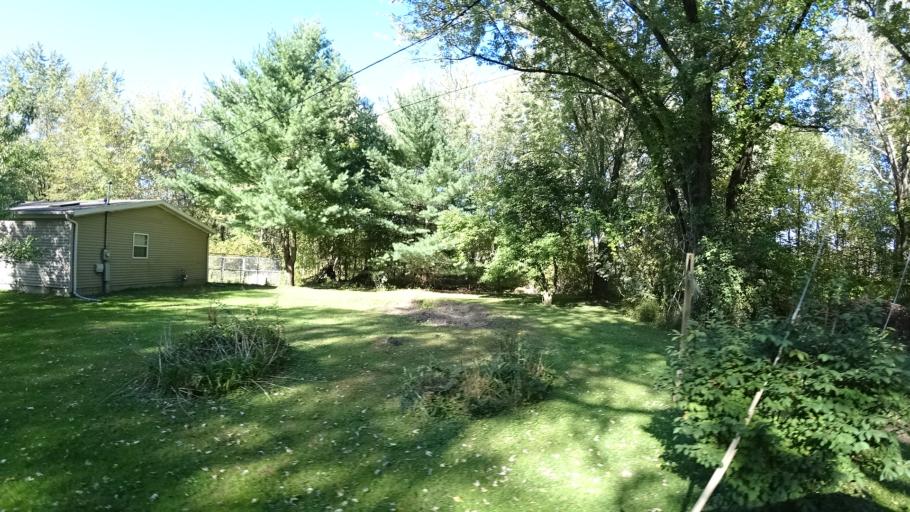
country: US
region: Indiana
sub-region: LaPorte County
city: Trail Creek
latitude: 41.7014
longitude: -86.8283
